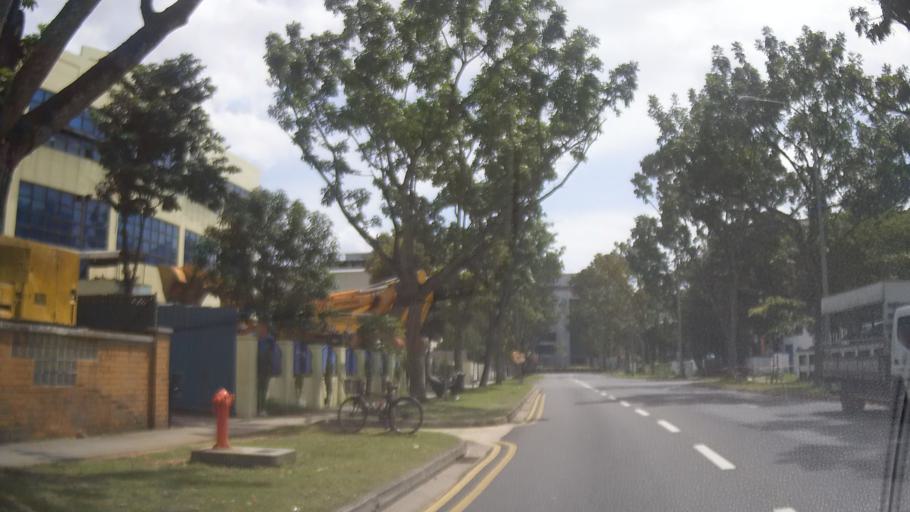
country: MY
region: Johor
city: Johor Bahru
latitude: 1.4100
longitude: 103.7434
